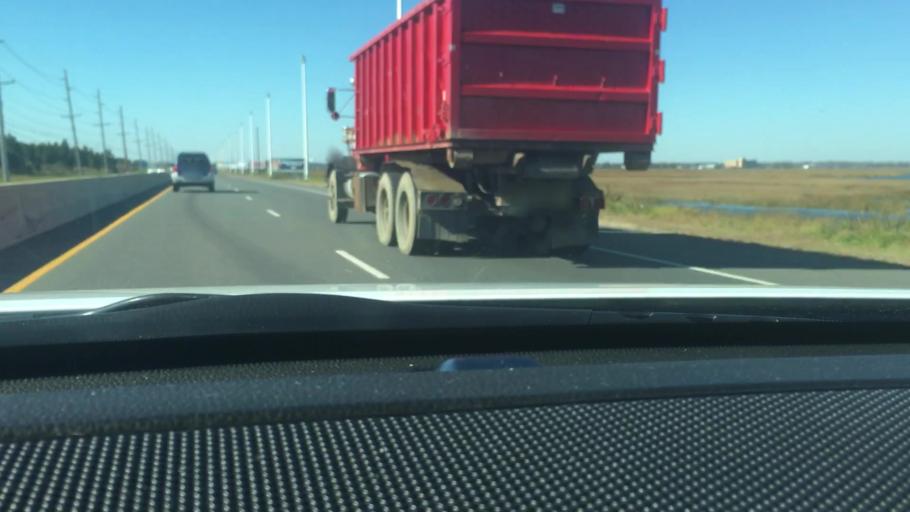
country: US
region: New Jersey
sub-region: Atlantic County
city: Absecon
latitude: 39.3875
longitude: -74.4726
